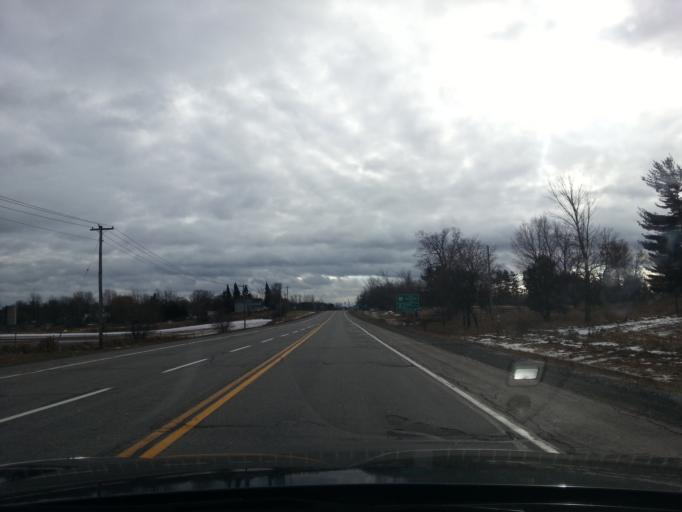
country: CA
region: Ontario
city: Bells Corners
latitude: 45.2216
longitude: -75.7175
